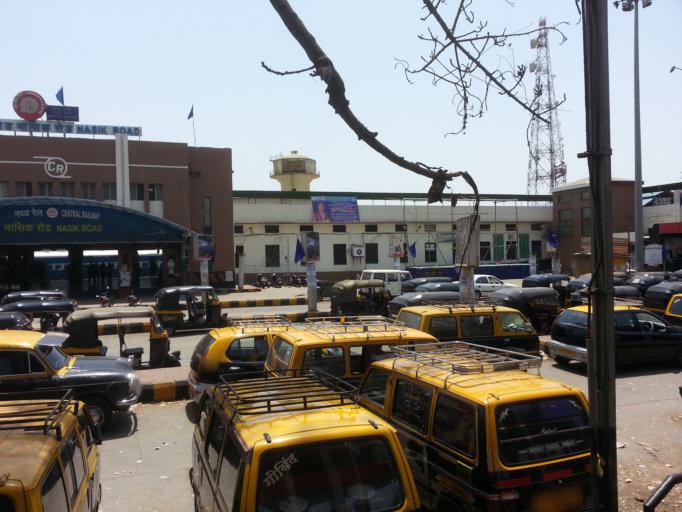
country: IN
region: Maharashtra
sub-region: Nashik Division
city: Deolali
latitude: 19.9481
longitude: 73.8417
